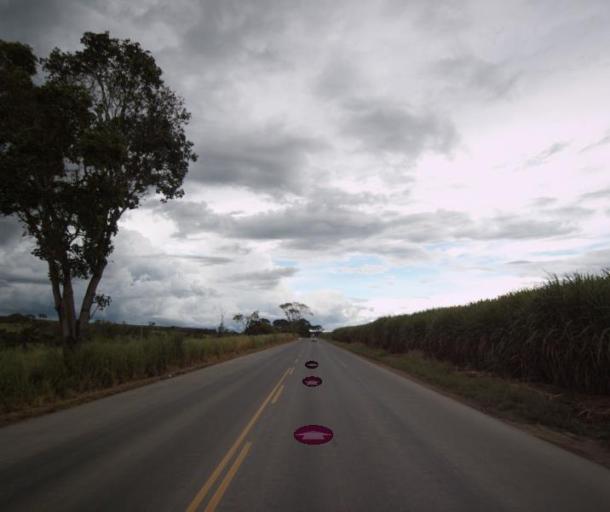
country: BR
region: Goias
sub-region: Itapaci
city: Itapaci
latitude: -14.9818
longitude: -49.3984
